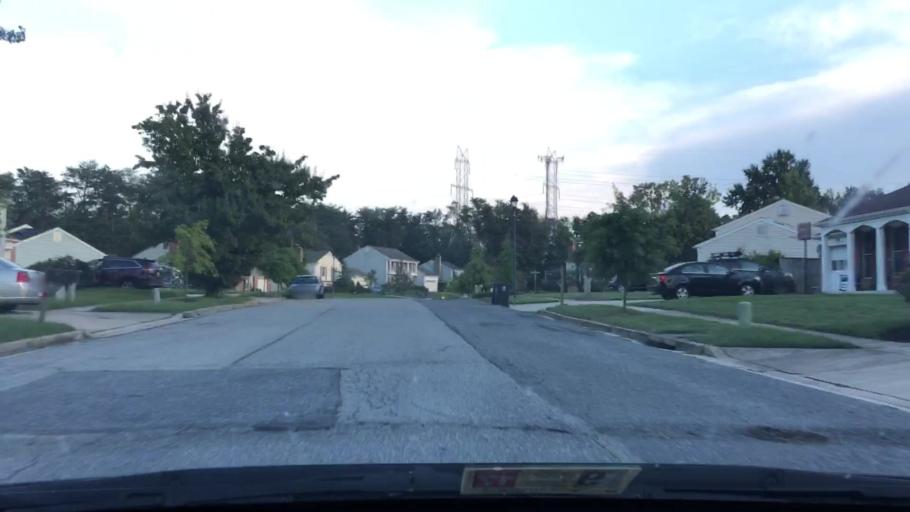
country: US
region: Maryland
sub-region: Prince George's County
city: South Laurel
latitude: 39.0515
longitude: -76.8293
